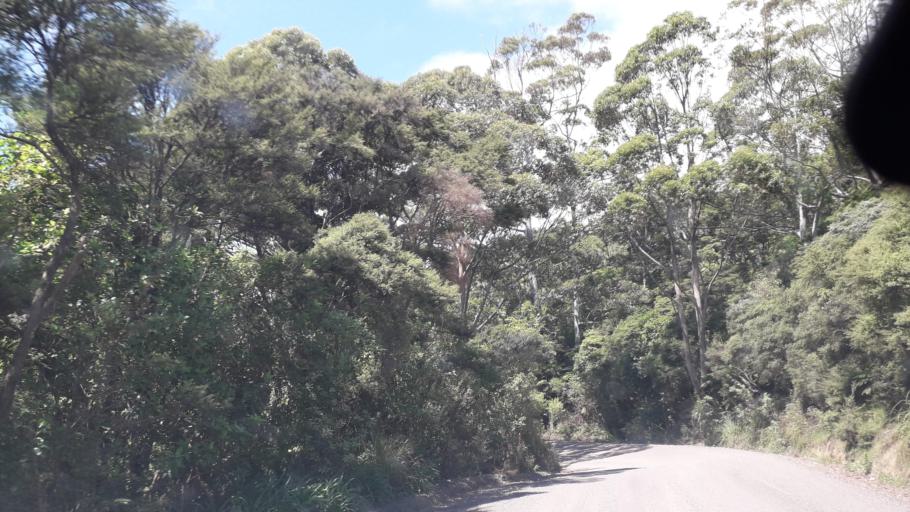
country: NZ
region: Northland
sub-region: Far North District
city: Paihia
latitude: -35.2387
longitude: 174.2545
